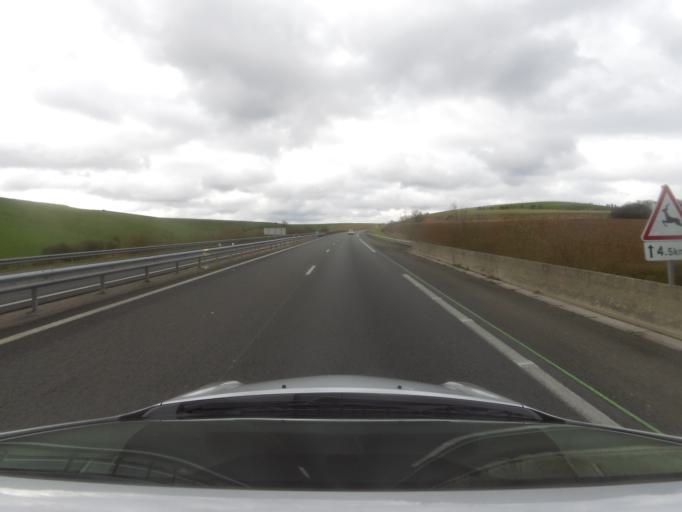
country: FR
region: Nord-Pas-de-Calais
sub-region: Departement du Pas-de-Calais
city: Neufchatel-Hardelot
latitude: 50.6058
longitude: 1.6543
